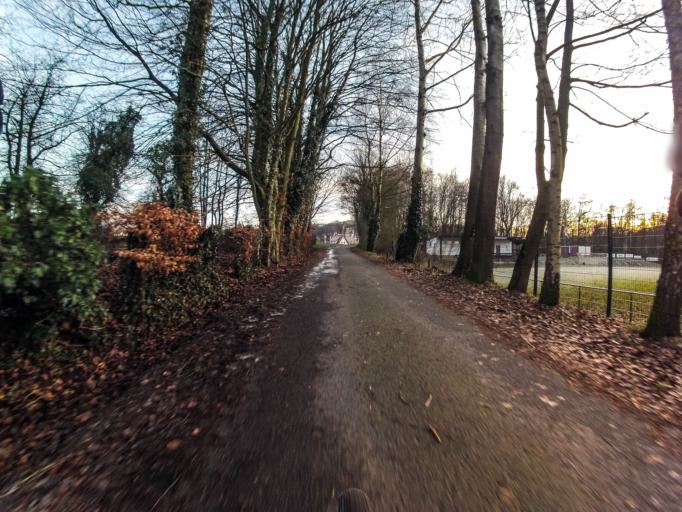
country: DE
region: North Rhine-Westphalia
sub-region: Regierungsbezirk Munster
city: Westerkappeln
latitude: 52.2823
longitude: 7.8374
